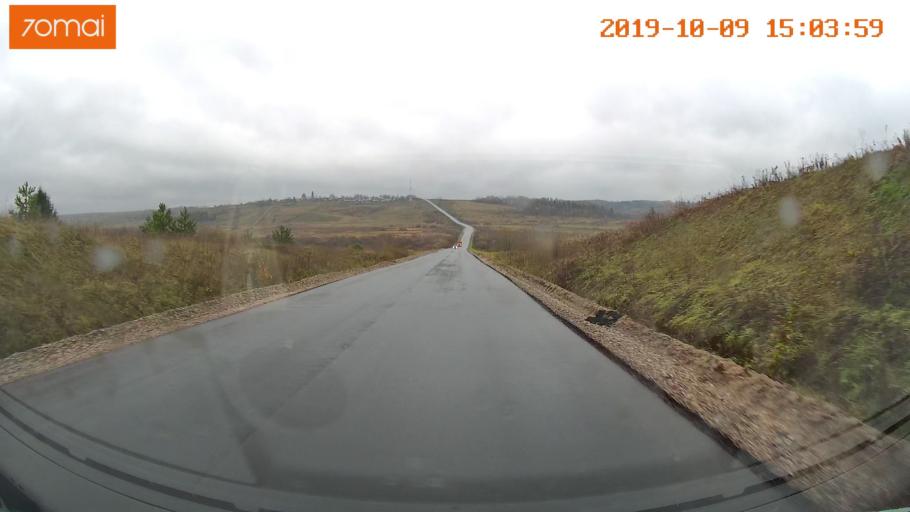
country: RU
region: Kostroma
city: Chistyye Bory
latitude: 58.2644
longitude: 41.6714
